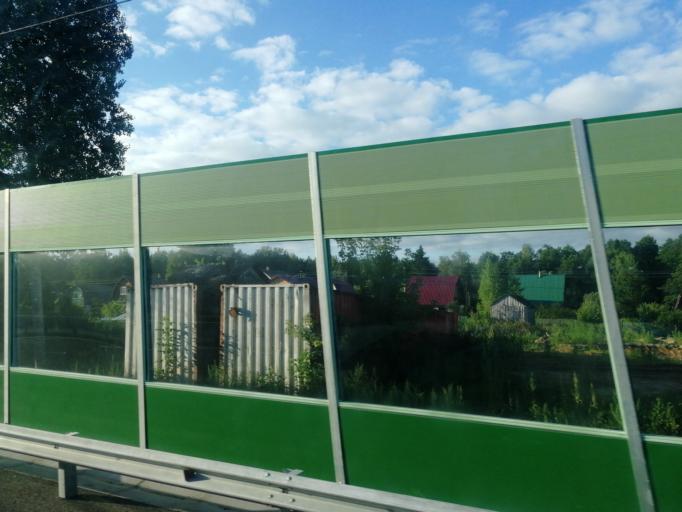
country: RU
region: Kaluga
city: Kaluga
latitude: 54.4550
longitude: 36.2874
